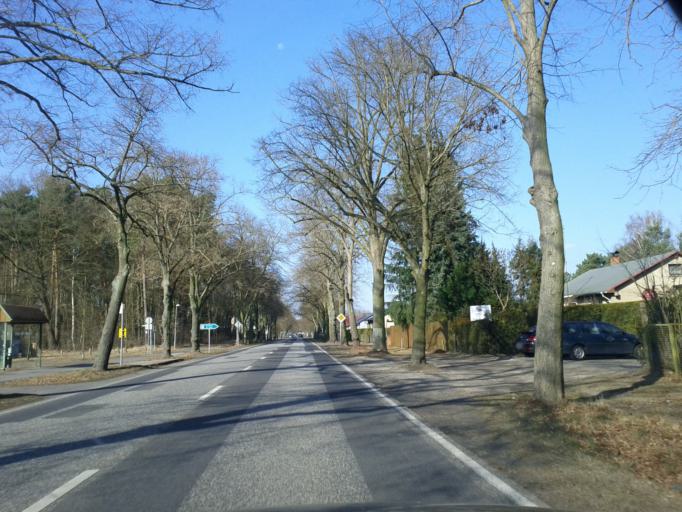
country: DE
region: Brandenburg
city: Spreenhagen
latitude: 52.3894
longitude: 13.9471
